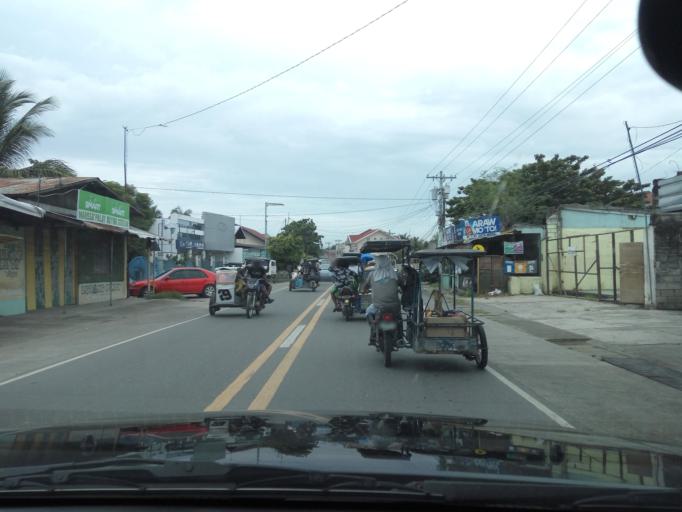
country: PH
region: Central Luzon
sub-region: Province of Nueva Ecija
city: Concepcion
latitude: 15.4501
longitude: 120.7930
